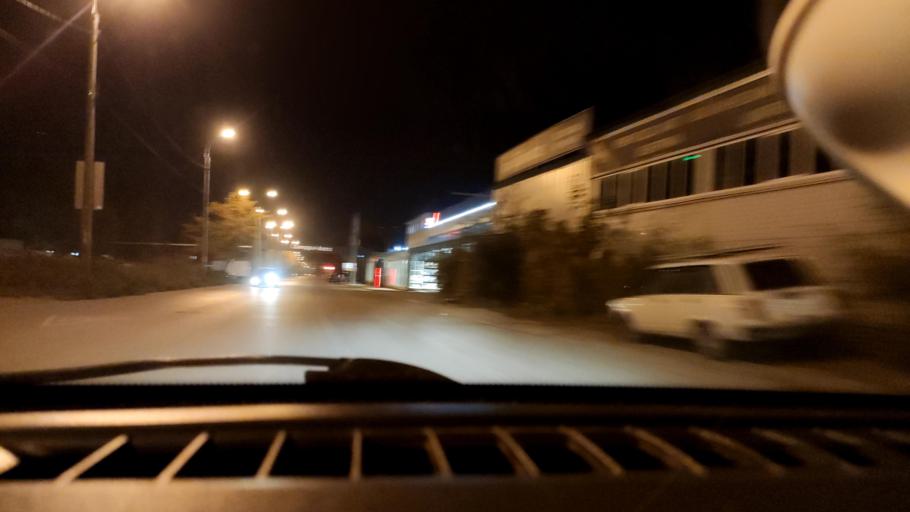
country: RU
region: Samara
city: Samara
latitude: 53.2397
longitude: 50.2495
